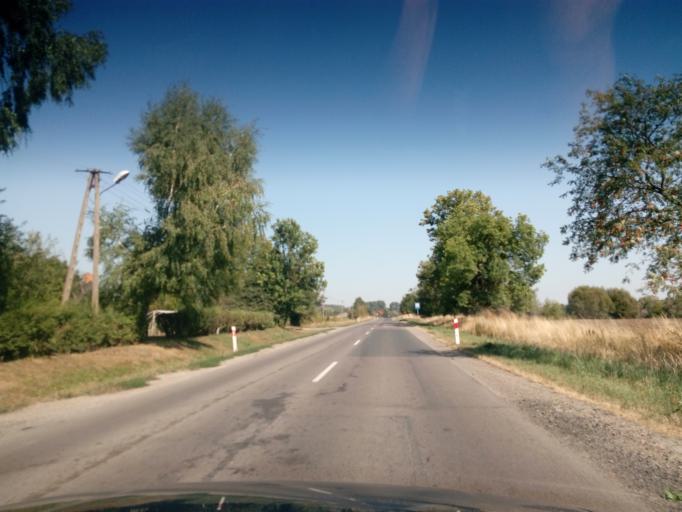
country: PL
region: Lublin Voivodeship
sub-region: Powiat hrubieszowski
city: Horodlo
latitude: 50.8416
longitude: 24.0010
